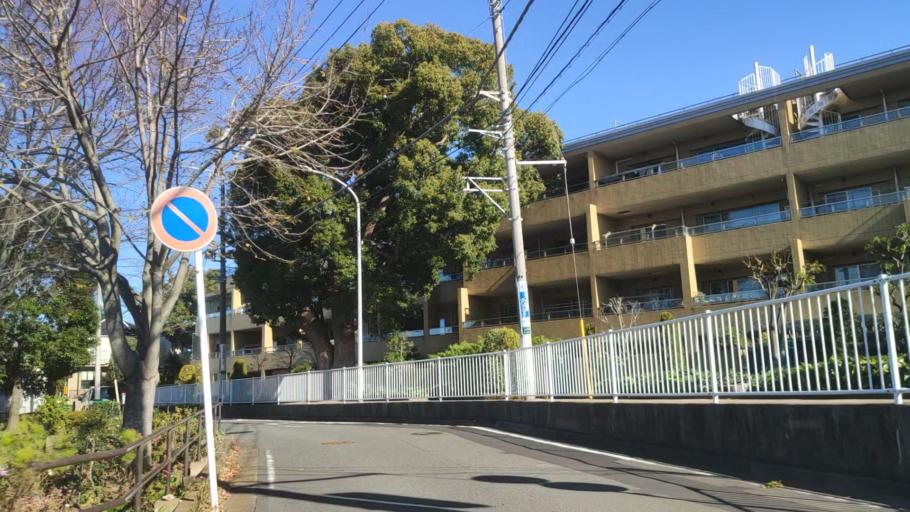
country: JP
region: Kanagawa
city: Yokohama
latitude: 35.4249
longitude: 139.6417
